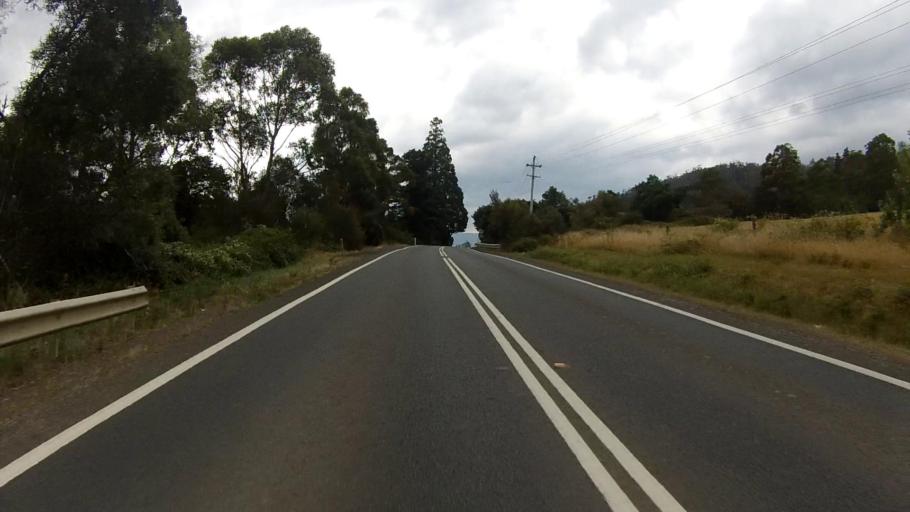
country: AU
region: Tasmania
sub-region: Huon Valley
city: Huonville
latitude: -43.0525
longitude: 147.0494
